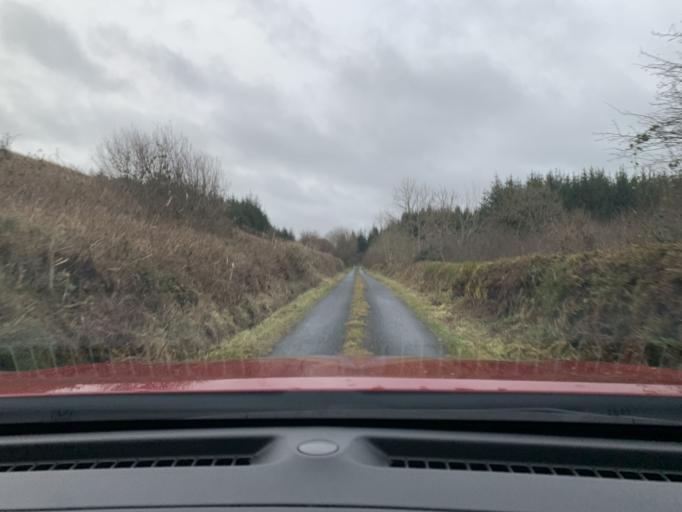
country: IE
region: Connaught
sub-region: Roscommon
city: Boyle
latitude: 54.0050
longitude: -8.3887
